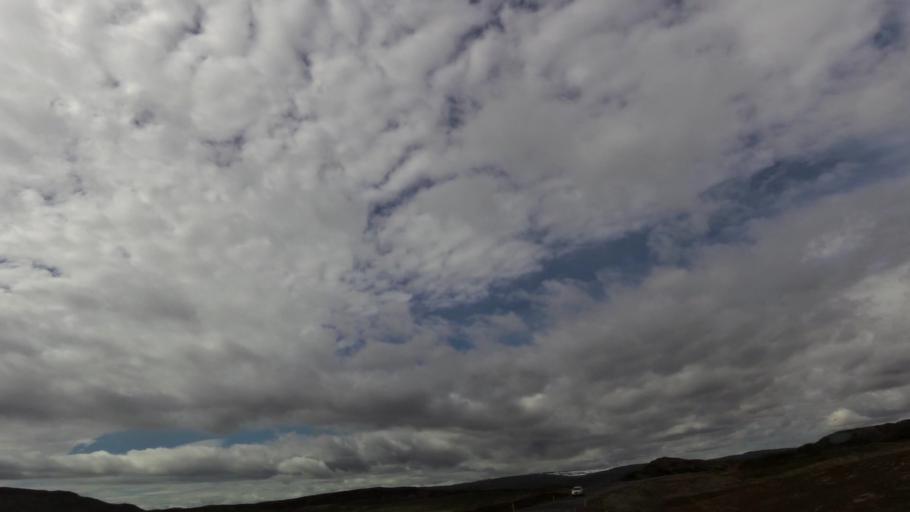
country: IS
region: West
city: Stykkisholmur
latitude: 65.5360
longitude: -22.0941
